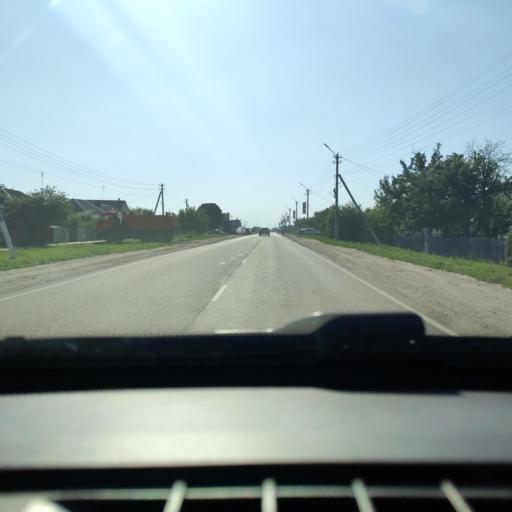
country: RU
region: Voronezj
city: Panino
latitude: 51.6444
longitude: 40.1246
